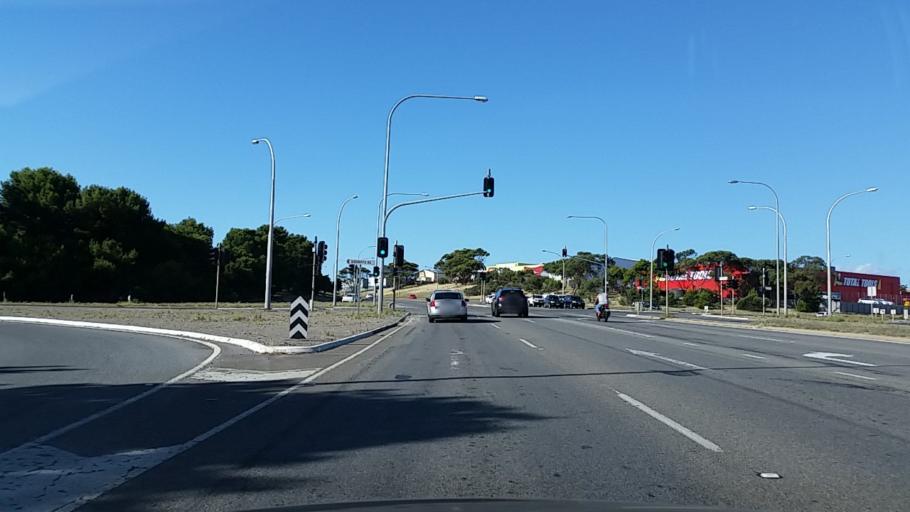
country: AU
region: South Australia
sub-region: Onkaparinga
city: Morphett Vale
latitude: -35.1070
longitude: 138.4986
